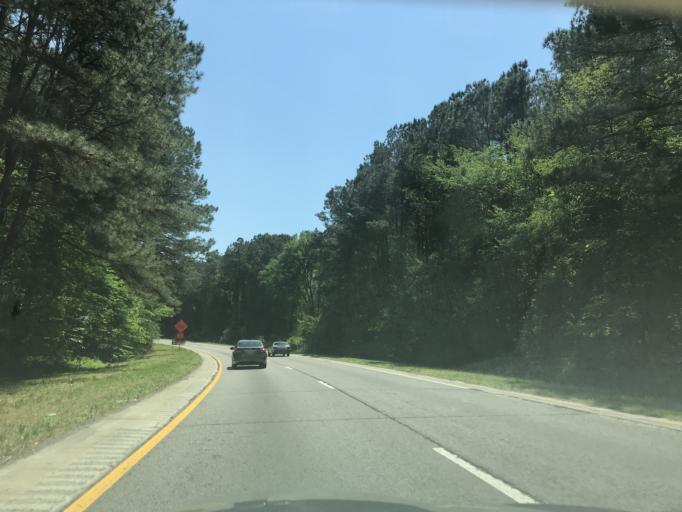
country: US
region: North Carolina
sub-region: Wake County
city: Garner
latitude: 35.7513
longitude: -78.5967
